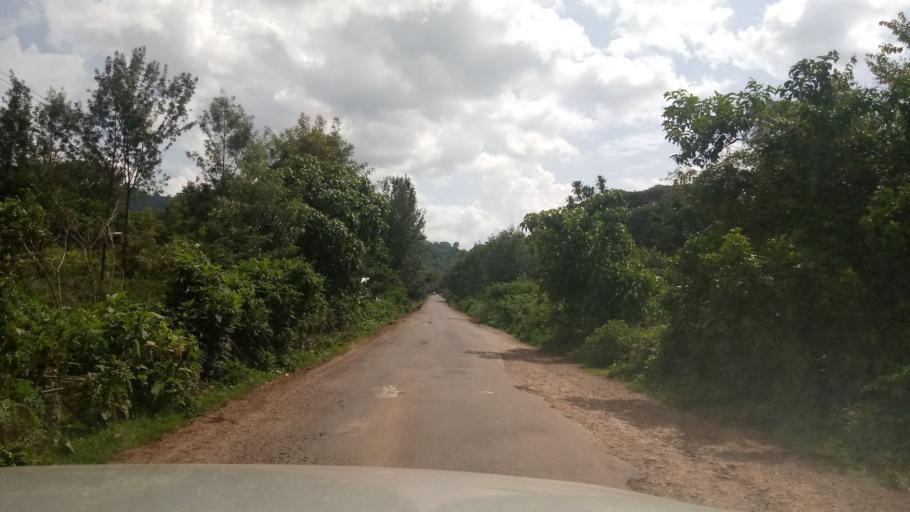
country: ET
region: Oromiya
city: Agaro
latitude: 7.9216
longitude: 36.5276
